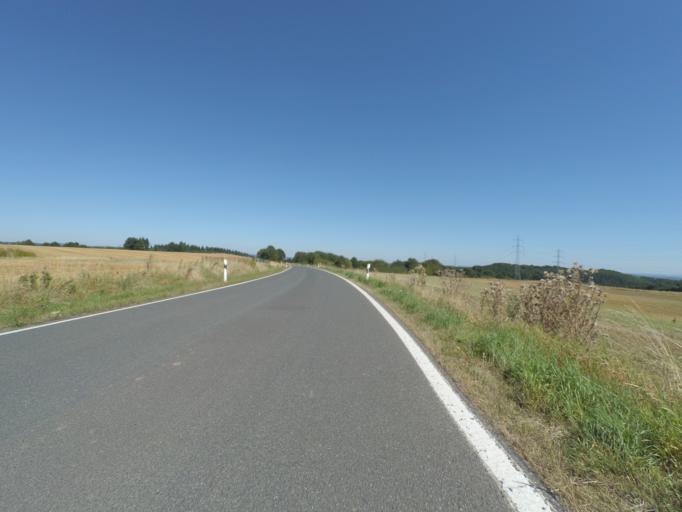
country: DE
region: Rheinland-Pfalz
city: Beuren
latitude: 50.0977
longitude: 7.0836
